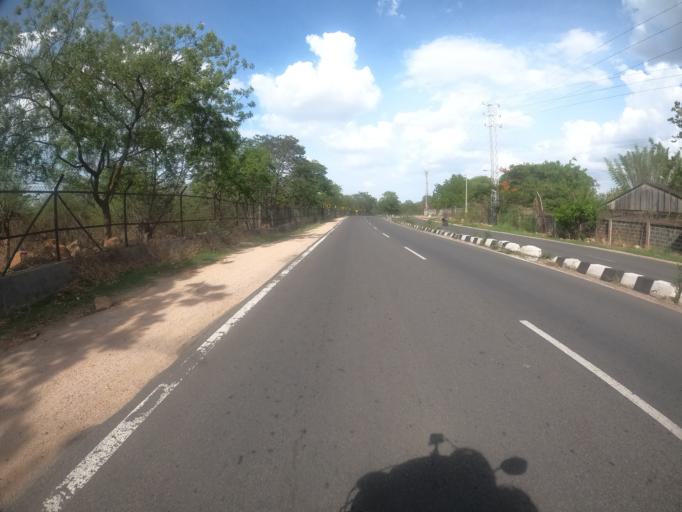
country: IN
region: Telangana
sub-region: Hyderabad
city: Hyderabad
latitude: 17.3538
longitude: 78.3423
